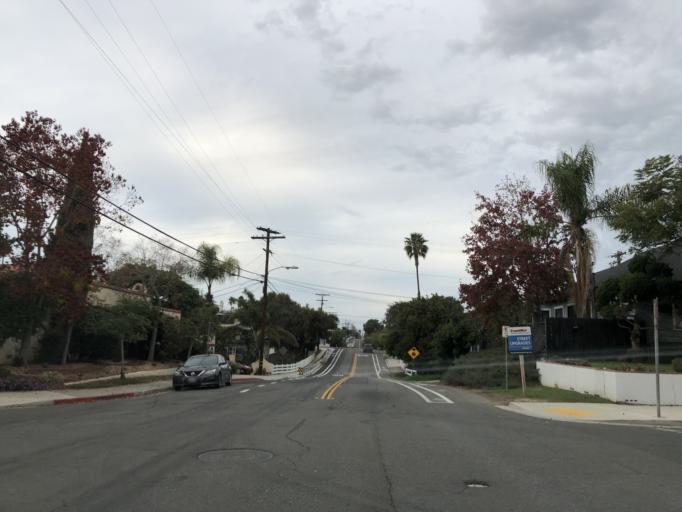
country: US
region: California
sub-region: San Diego County
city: San Diego
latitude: 32.7421
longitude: -117.1512
